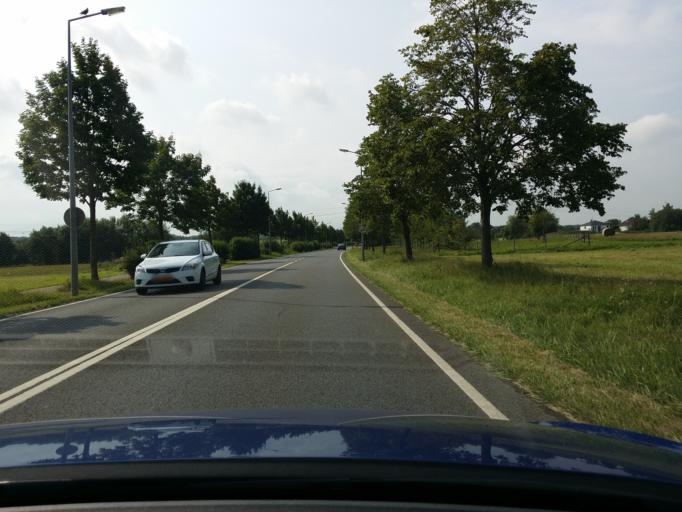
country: LU
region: Luxembourg
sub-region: Canton de Luxembourg
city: Bertrange
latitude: 49.6072
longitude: 6.0591
